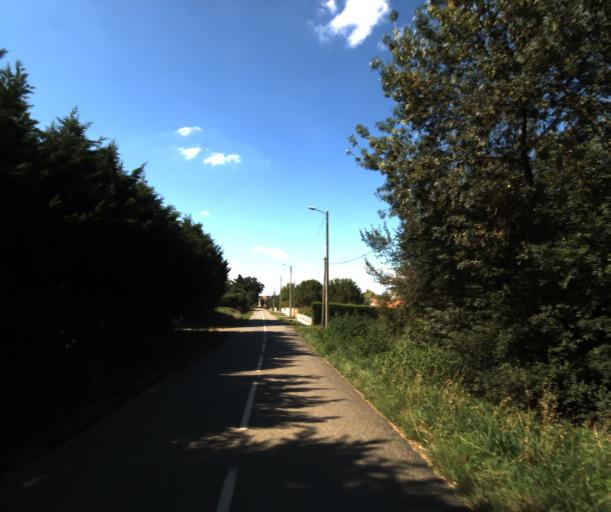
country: FR
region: Midi-Pyrenees
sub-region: Departement de la Haute-Garonne
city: Fonsorbes
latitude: 43.5033
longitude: 1.2201
